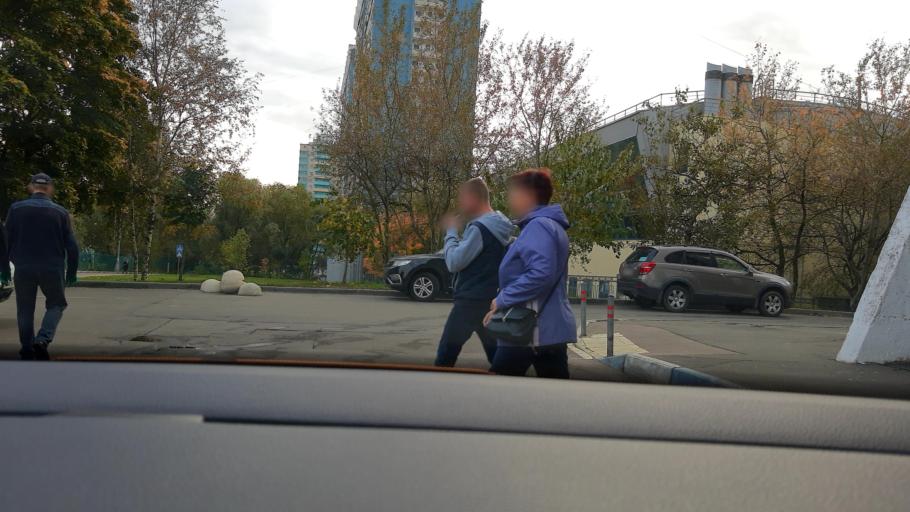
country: RU
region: Moscow
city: Yasenevo
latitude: 55.6012
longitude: 37.5327
